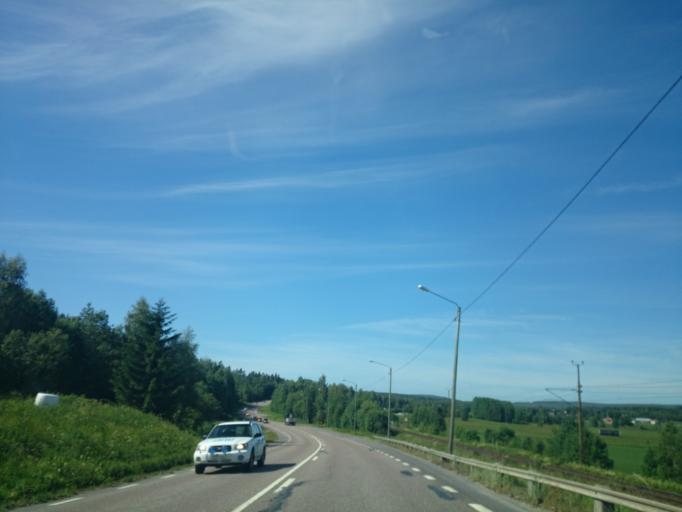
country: SE
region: Vaesternorrland
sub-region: Sundsvalls Kommun
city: Vi
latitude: 62.3888
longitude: 17.1789
